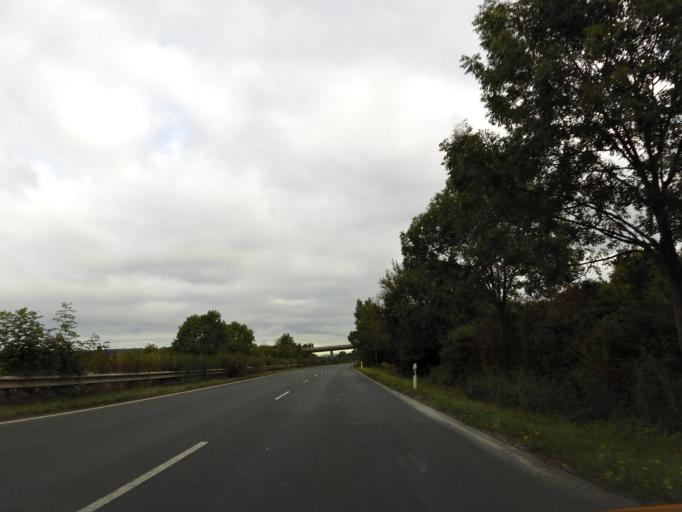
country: DE
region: Lower Saxony
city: Bovenden
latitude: 51.5630
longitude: 9.9199
